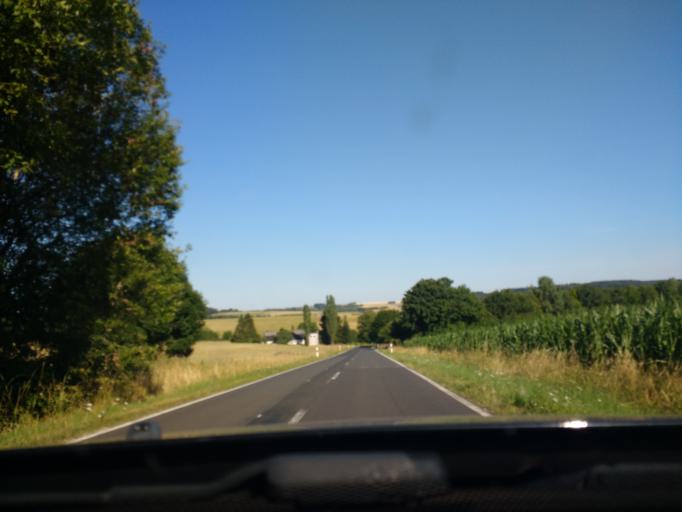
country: DE
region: Rheinland-Pfalz
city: Meisburg
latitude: 50.1083
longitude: 6.6980
